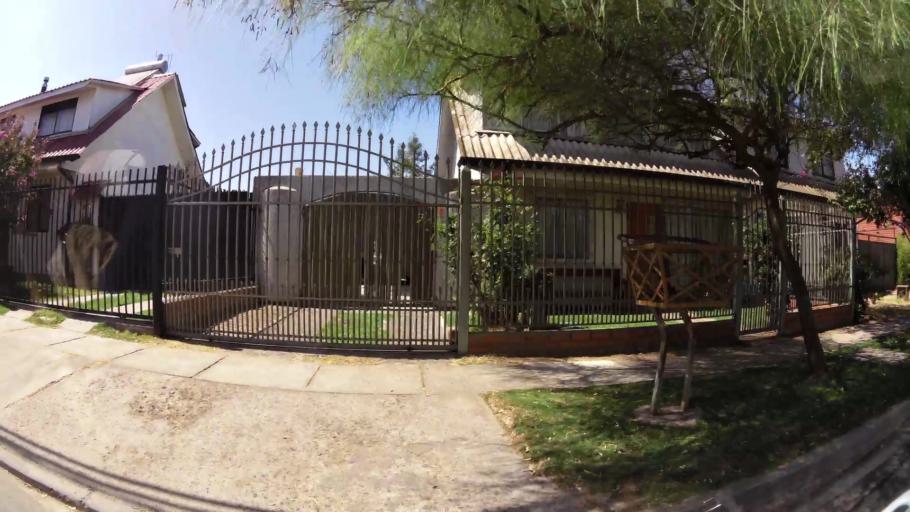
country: CL
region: Maule
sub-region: Provincia de Talca
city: Talca
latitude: -35.4224
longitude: -71.6275
